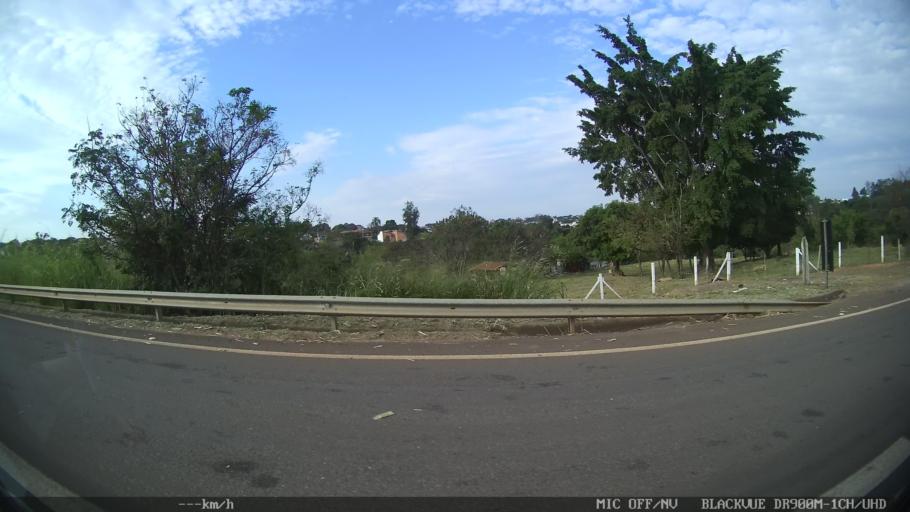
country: BR
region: Sao Paulo
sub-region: Cosmopolis
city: Cosmopolis
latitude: -22.6443
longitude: -47.2082
